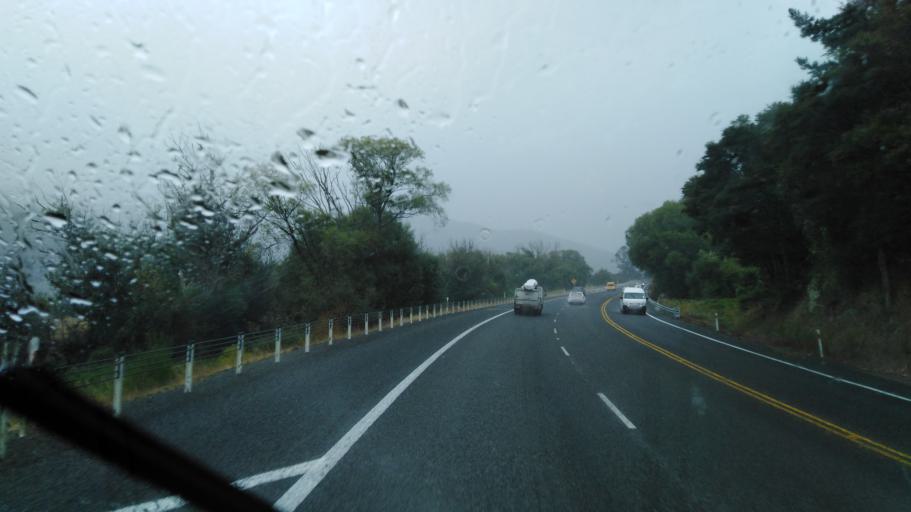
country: NZ
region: Marlborough
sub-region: Marlborough District
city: Picton
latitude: -41.3790
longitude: 173.9469
